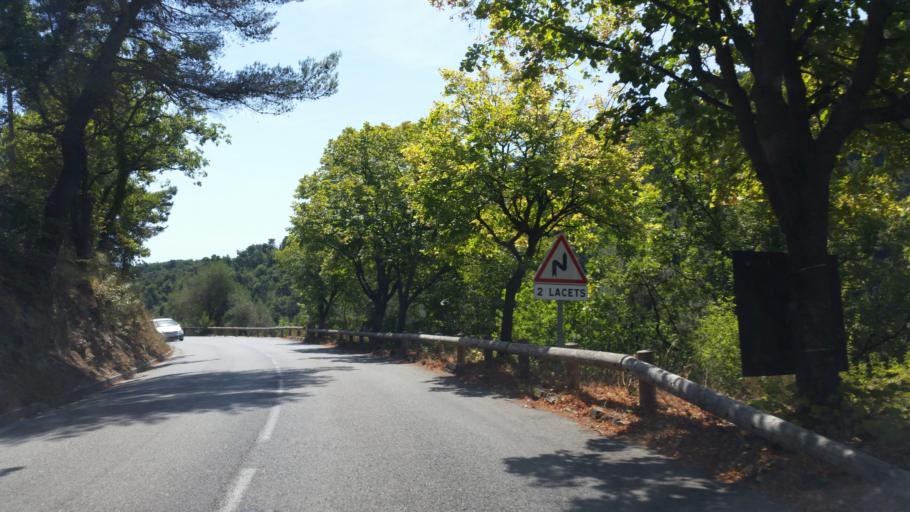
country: FR
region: Provence-Alpes-Cote d'Azur
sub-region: Departement des Alpes-Maritimes
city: Sainte-Agnes
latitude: 43.8334
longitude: 7.4712
